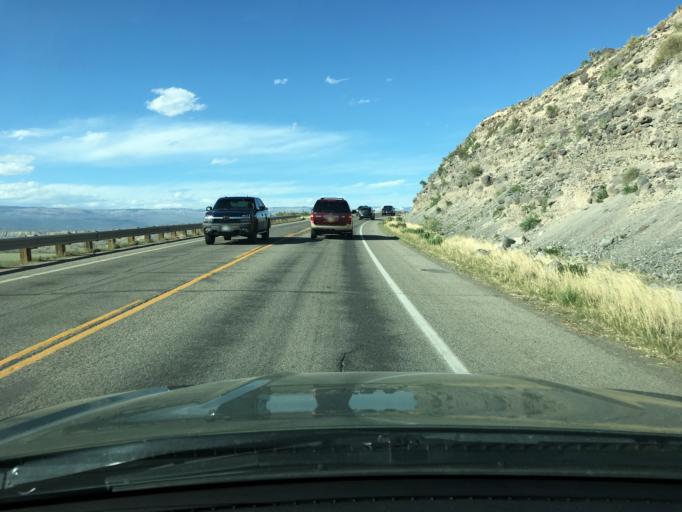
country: US
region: Colorado
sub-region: Delta County
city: Orchard City
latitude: 38.7826
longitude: -107.9968
